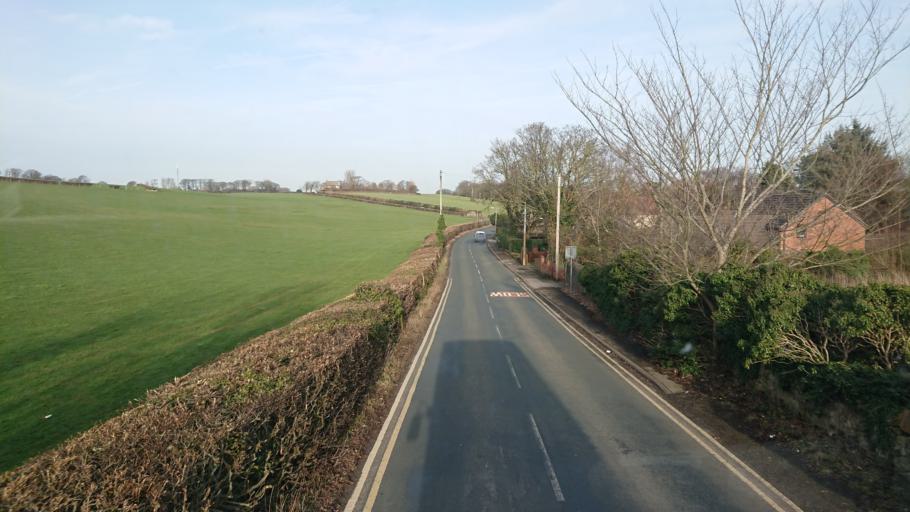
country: GB
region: England
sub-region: Lancashire
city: Bolton le Sands
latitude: 54.0694
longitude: -2.7912
